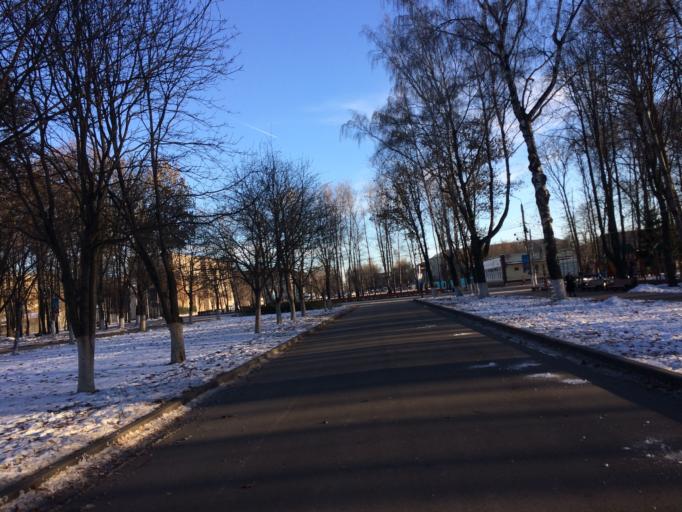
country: RU
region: Tula
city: Tula
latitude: 54.1782
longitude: 37.5918
